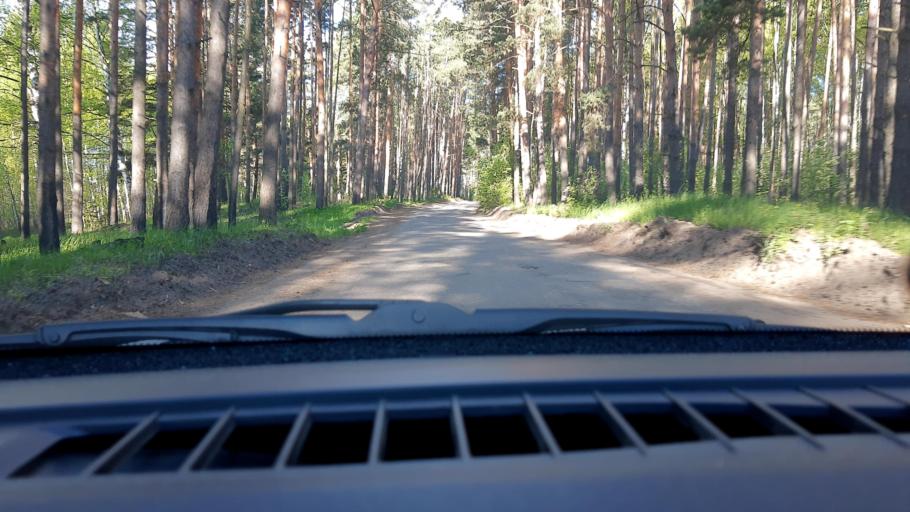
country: RU
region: Nizjnij Novgorod
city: Sitniki
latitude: 56.4166
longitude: 44.0443
